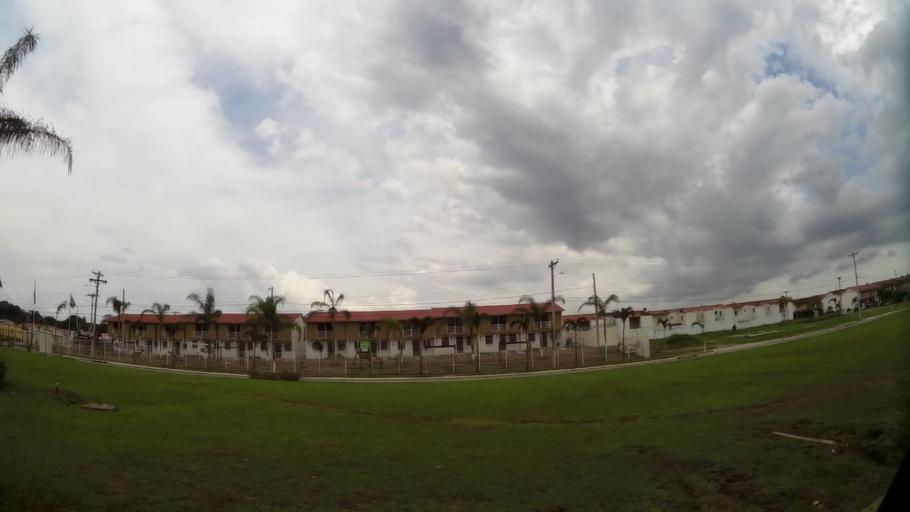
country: PA
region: Panama
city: Cabra Numero Uno
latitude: 9.1198
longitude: -79.3197
